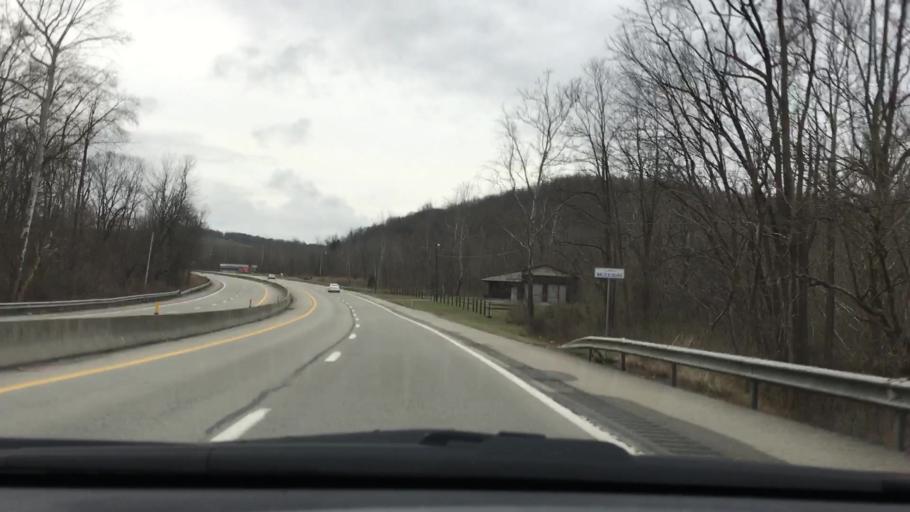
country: US
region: Pennsylvania
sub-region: Fayette County
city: Oliver
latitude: 39.9899
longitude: -79.7657
